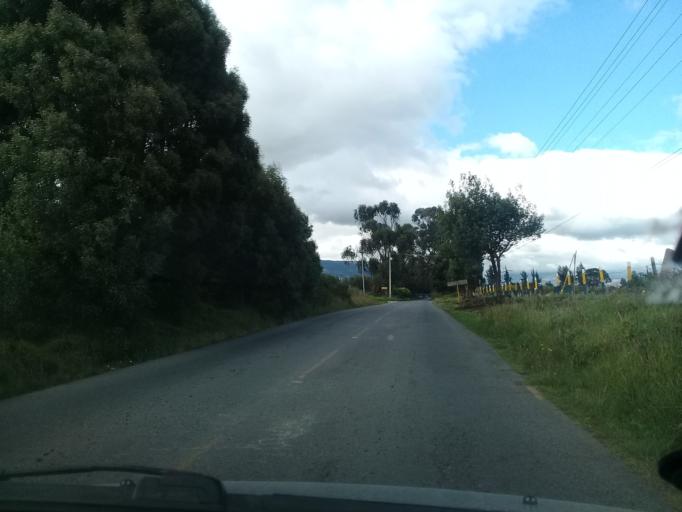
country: CO
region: Cundinamarca
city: Subachoque
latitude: 4.8986
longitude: -74.1937
